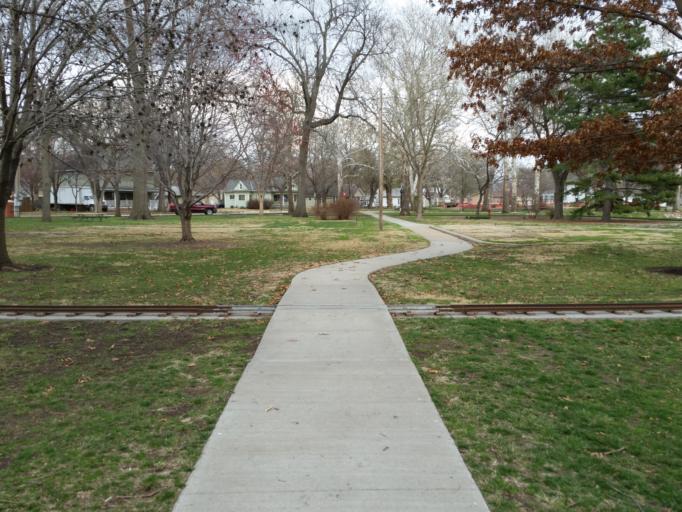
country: US
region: Kansas
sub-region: Pottawatomie County
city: Wamego
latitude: 39.2028
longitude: -96.3020
